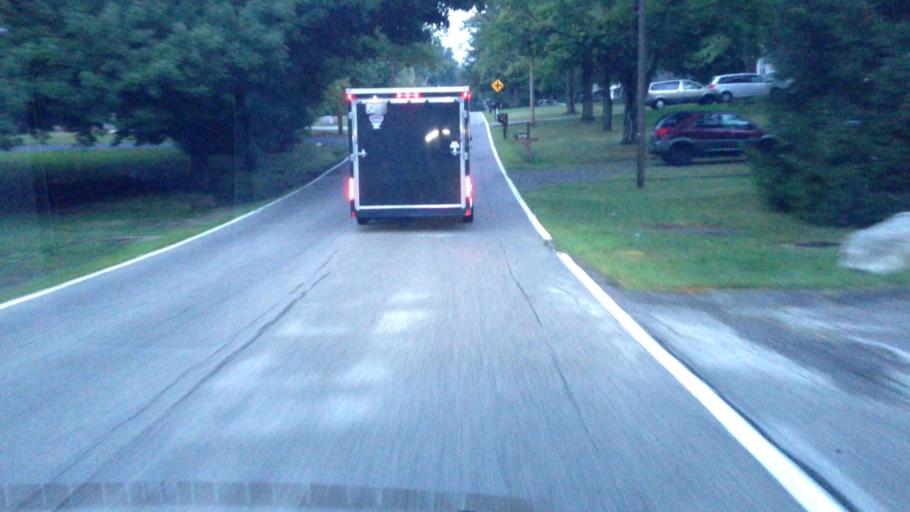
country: US
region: Ohio
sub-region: Summit County
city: Silver Lake
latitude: 41.1752
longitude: -81.4549
